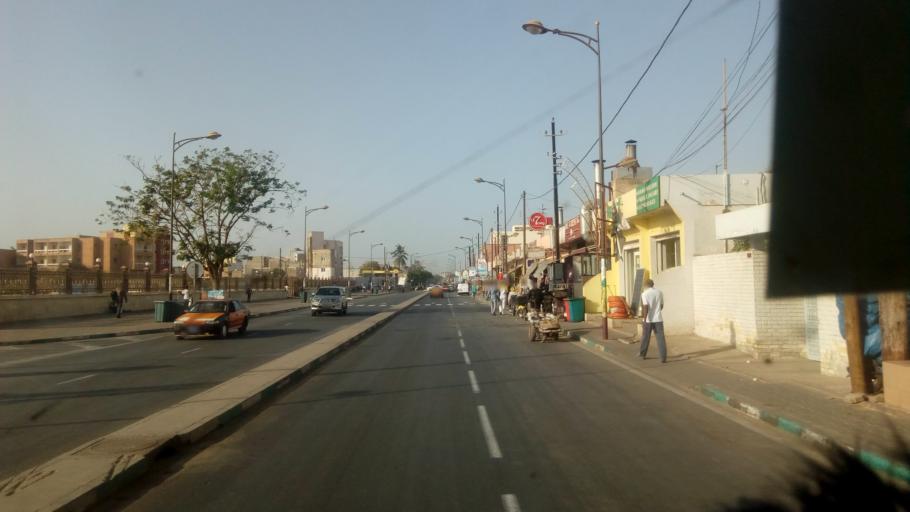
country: SN
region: Dakar
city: Dakar
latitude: 14.7004
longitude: -17.4471
